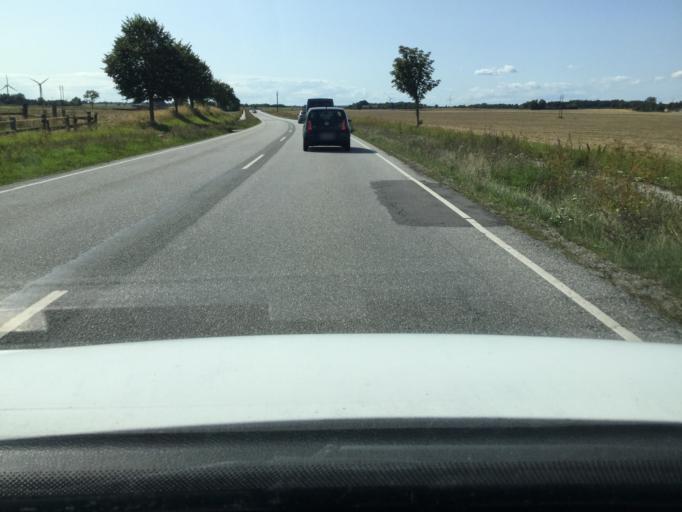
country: DK
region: Zealand
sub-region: Lolland Kommune
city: Nakskov
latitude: 54.8138
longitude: 11.1885
